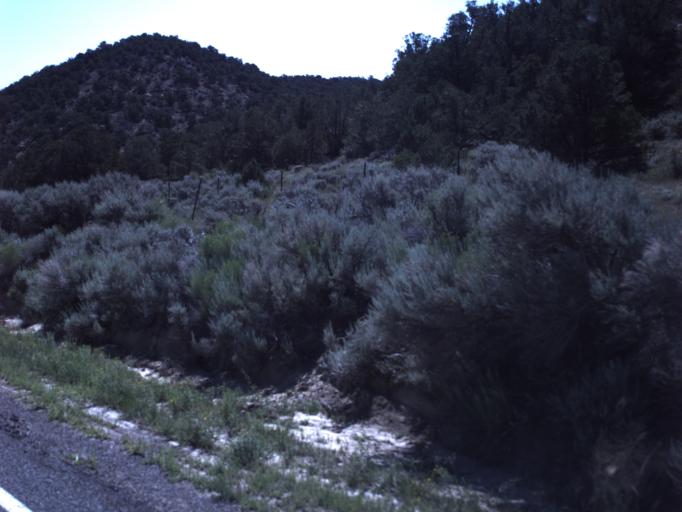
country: US
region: Utah
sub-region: Wayne County
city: Loa
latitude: 38.7571
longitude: -111.4145
